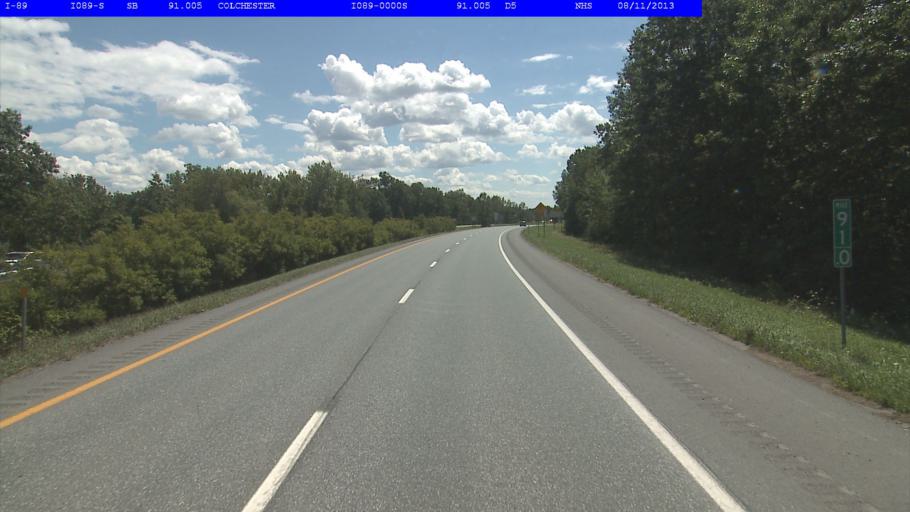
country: US
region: Vermont
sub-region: Chittenden County
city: Winooski
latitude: 44.5008
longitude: -73.1745
